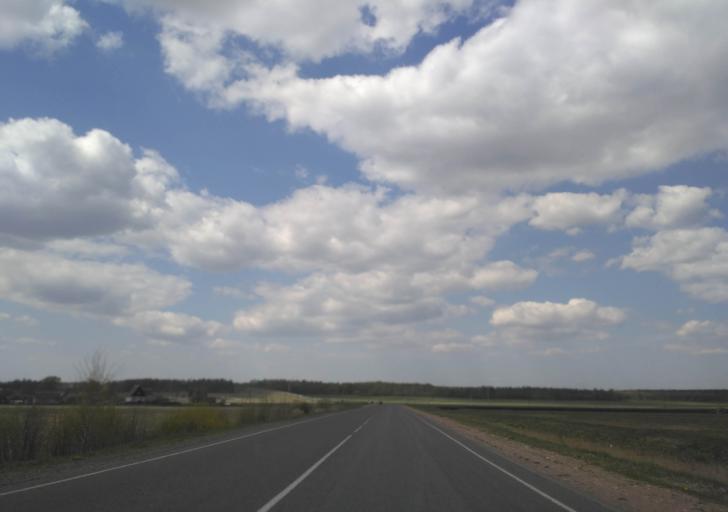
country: BY
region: Minsk
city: Vilyeyka
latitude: 54.5194
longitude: 26.9745
